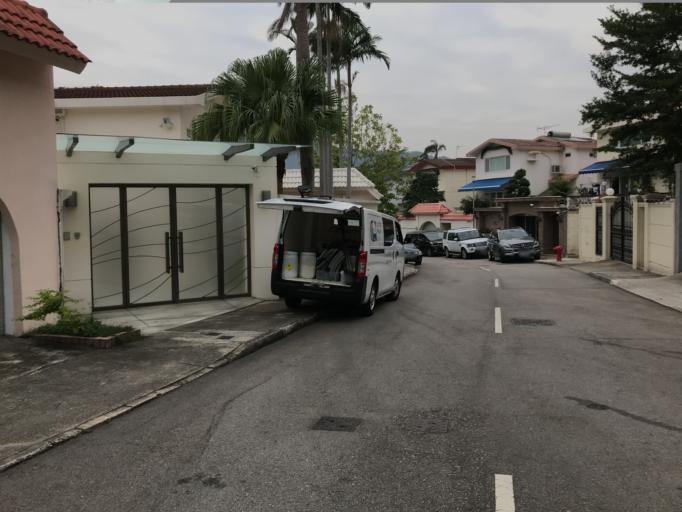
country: HK
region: Tai Po
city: Tai Po
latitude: 22.4638
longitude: 114.1573
